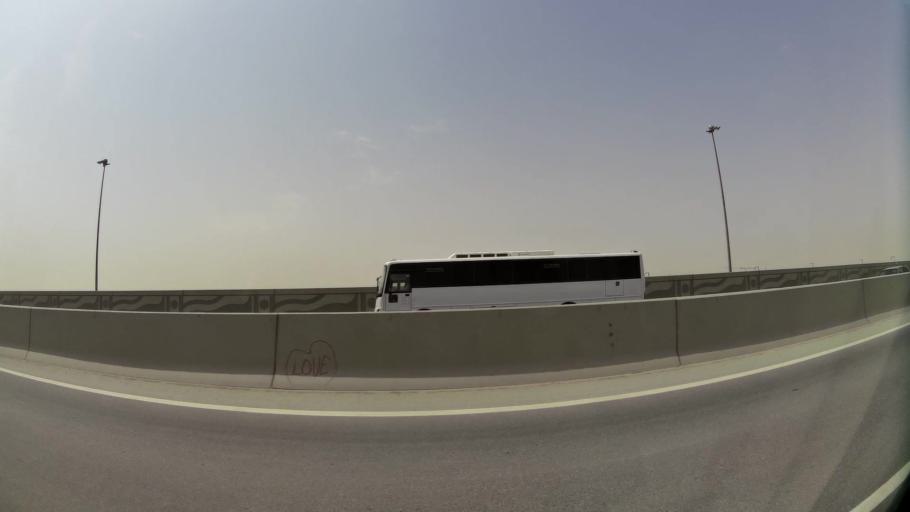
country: QA
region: Baladiyat ar Rayyan
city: Ar Rayyan
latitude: 25.2033
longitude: 51.4477
